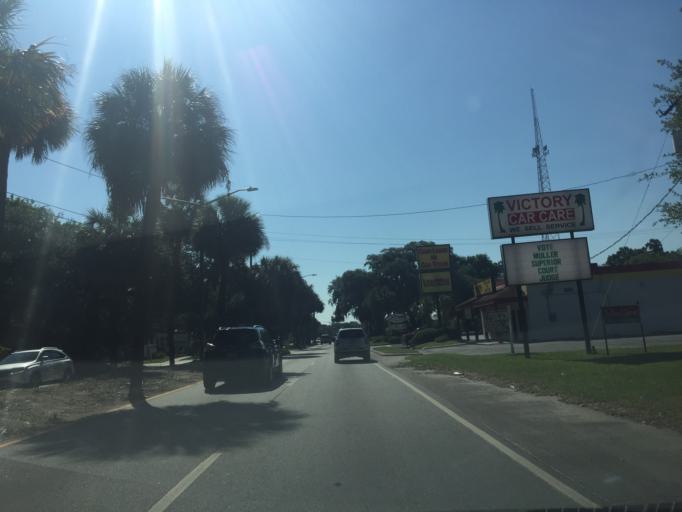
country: US
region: Georgia
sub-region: Chatham County
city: Thunderbolt
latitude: 32.0453
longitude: -81.0750
